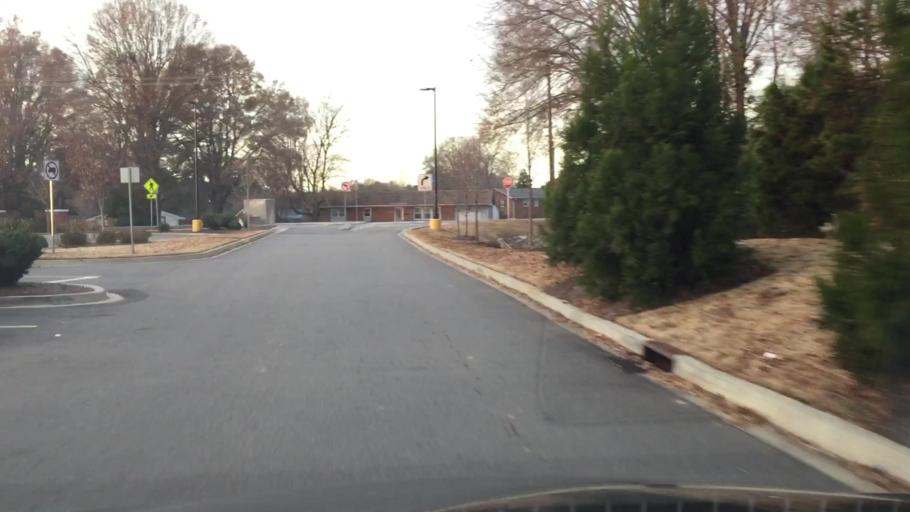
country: US
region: North Carolina
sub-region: Iredell County
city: Mooresville
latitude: 35.5780
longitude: -80.7923
